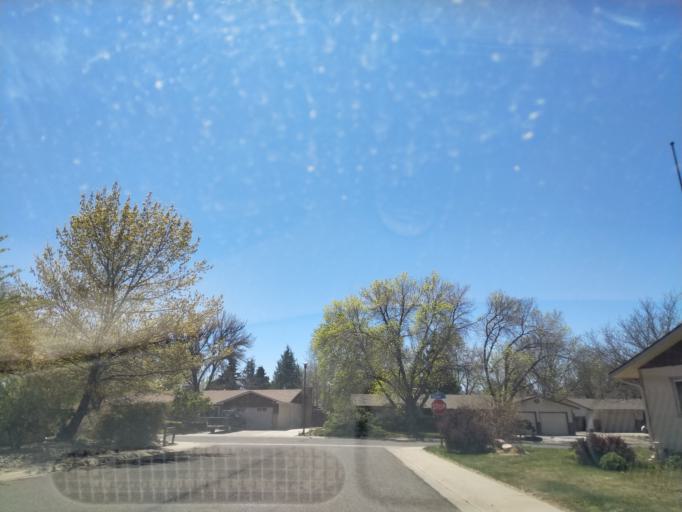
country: US
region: Colorado
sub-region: Mesa County
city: Grand Junction
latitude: 39.0950
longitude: -108.5413
